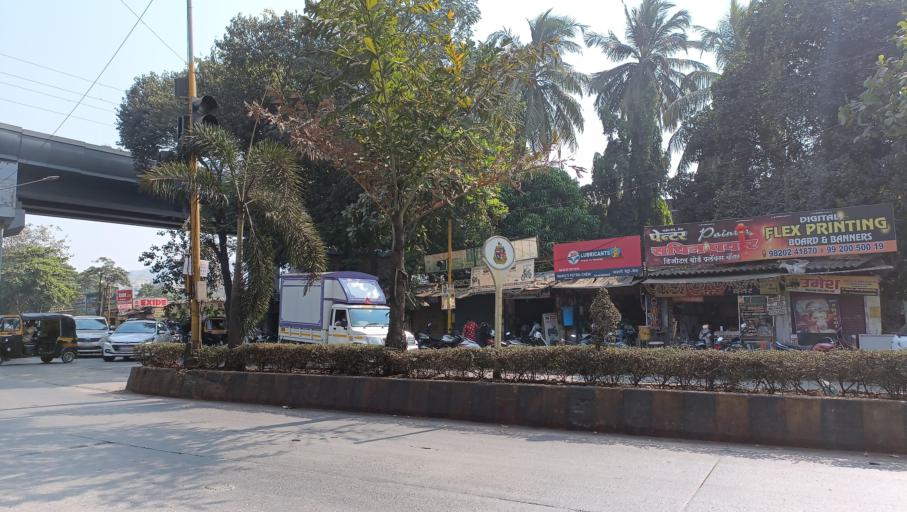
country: IN
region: Maharashtra
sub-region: Mumbai Suburban
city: Borivli
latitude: 19.2556
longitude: 72.8683
